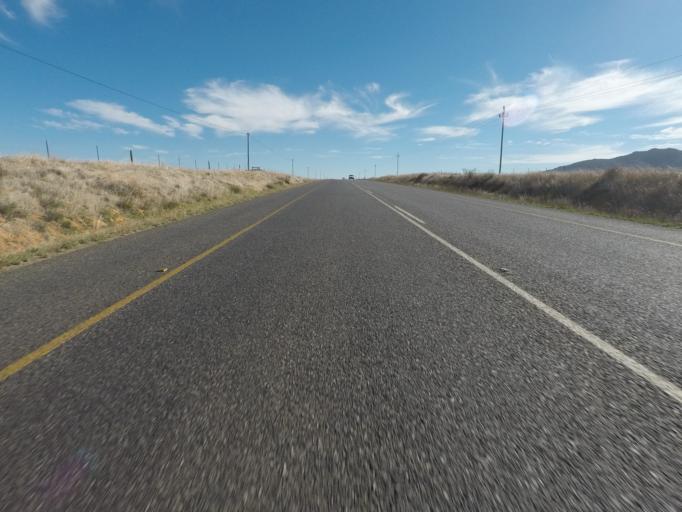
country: ZA
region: Western Cape
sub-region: West Coast District Municipality
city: Malmesbury
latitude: -33.6114
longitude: 18.7276
